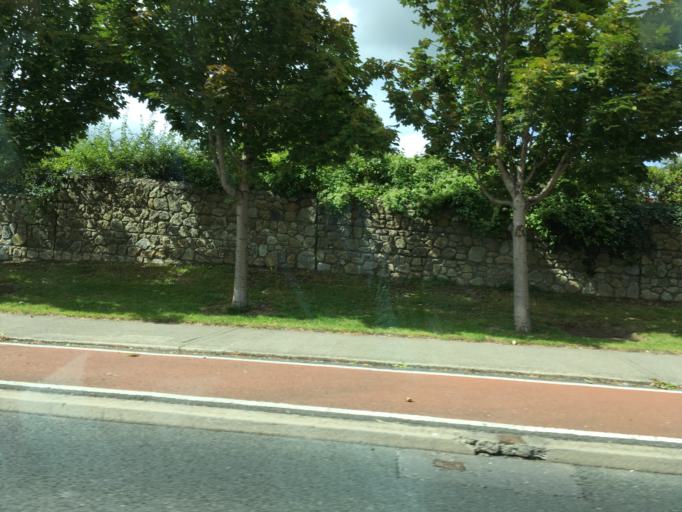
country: IE
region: Leinster
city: Little Bray
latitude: 53.1914
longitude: -6.1240
